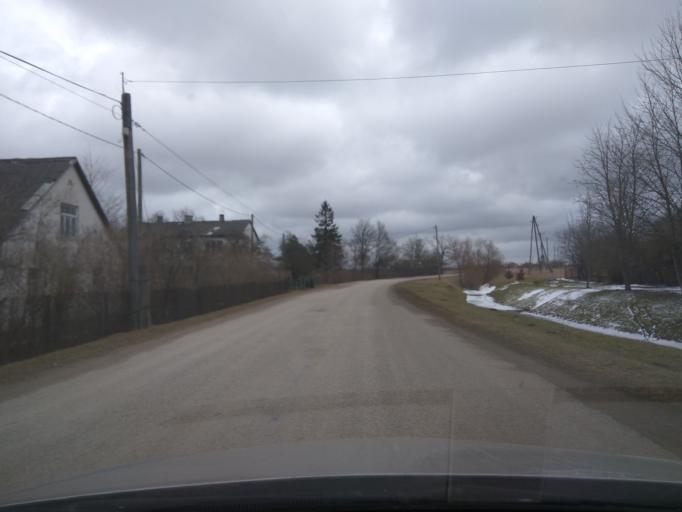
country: LV
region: Ventspils
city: Ventspils
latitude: 57.3321
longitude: 21.6521
